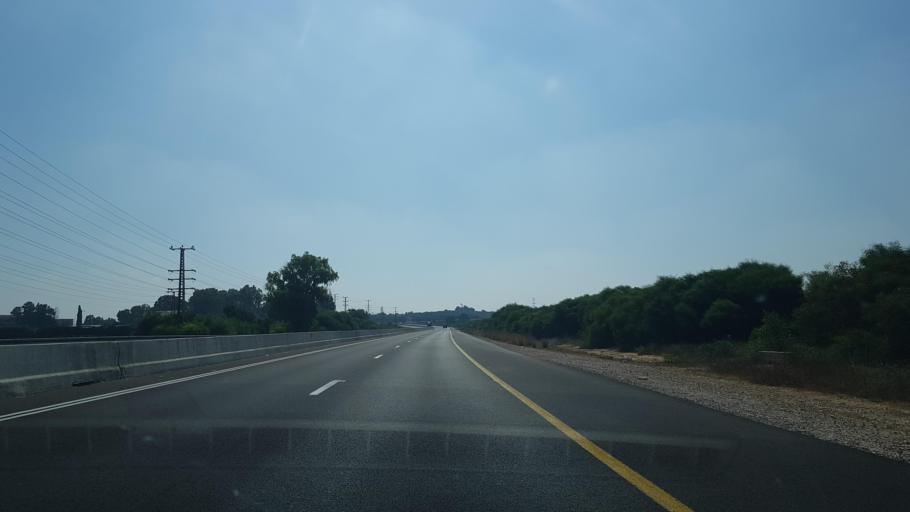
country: IL
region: Southern District
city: Ashqelon
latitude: 31.6886
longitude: 34.6678
